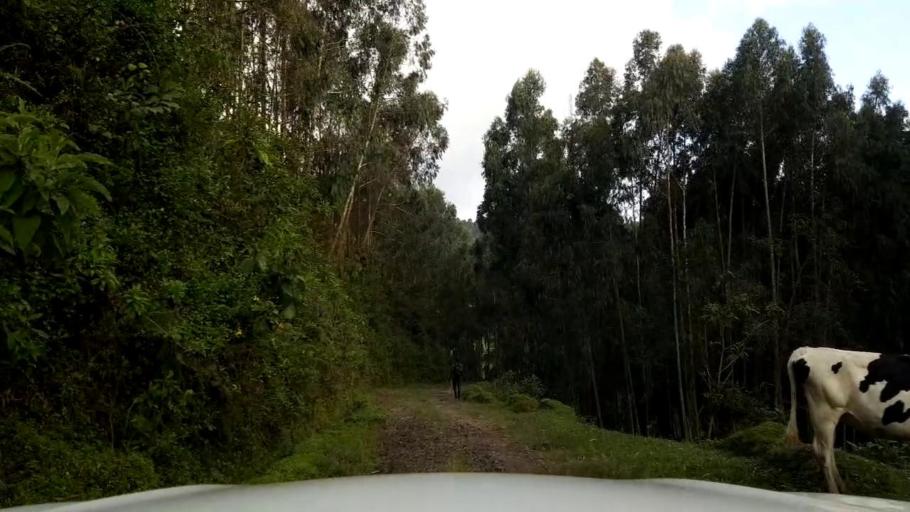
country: RW
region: Western Province
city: Gisenyi
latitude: -1.7234
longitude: 29.4338
